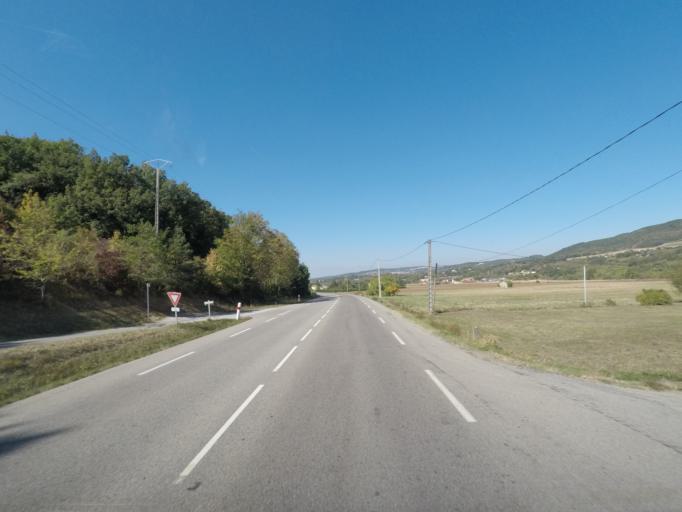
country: FR
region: Rhone-Alpes
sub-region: Departement de la Drome
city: Aouste-sur-Sye
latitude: 44.7071
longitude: 5.0808
